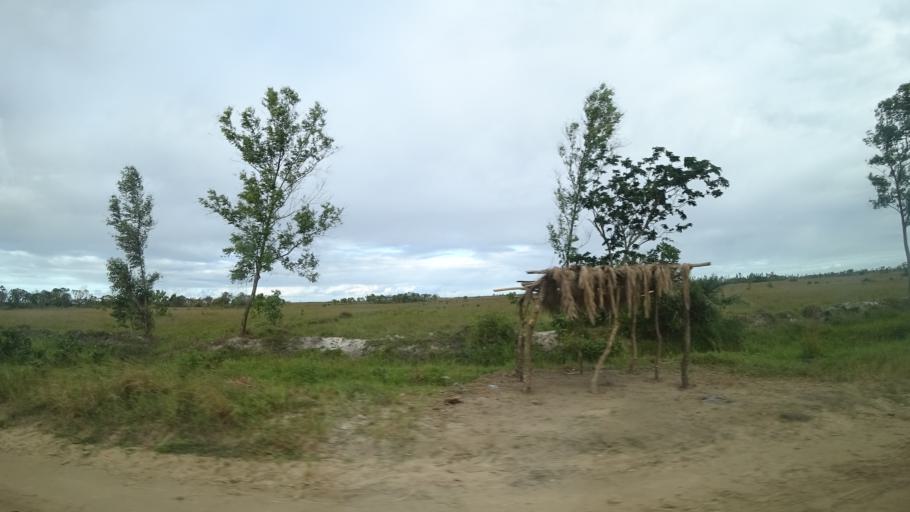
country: MZ
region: Sofala
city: Beira
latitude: -19.7218
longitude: 34.9977
